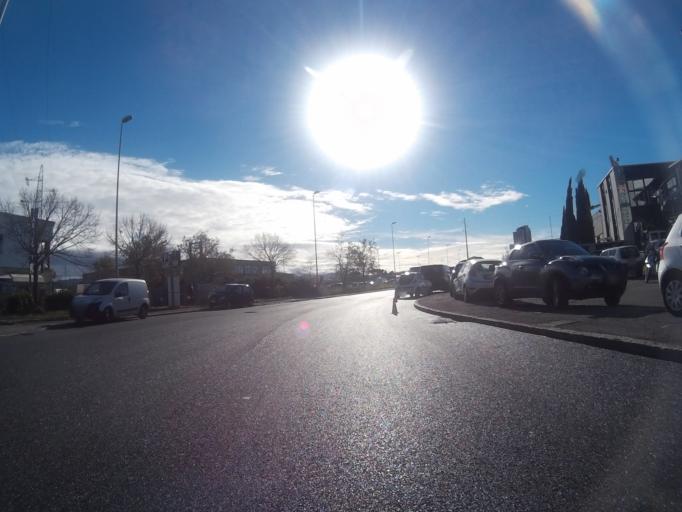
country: IT
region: Tuscany
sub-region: Provincia di Livorno
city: Livorno
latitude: 43.5664
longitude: 10.3419
